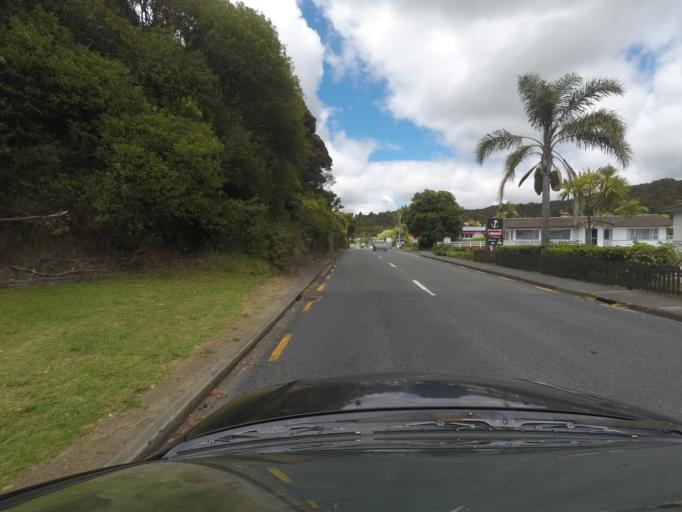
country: NZ
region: Northland
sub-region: Far North District
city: Paihia
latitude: -35.2855
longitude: 174.0968
